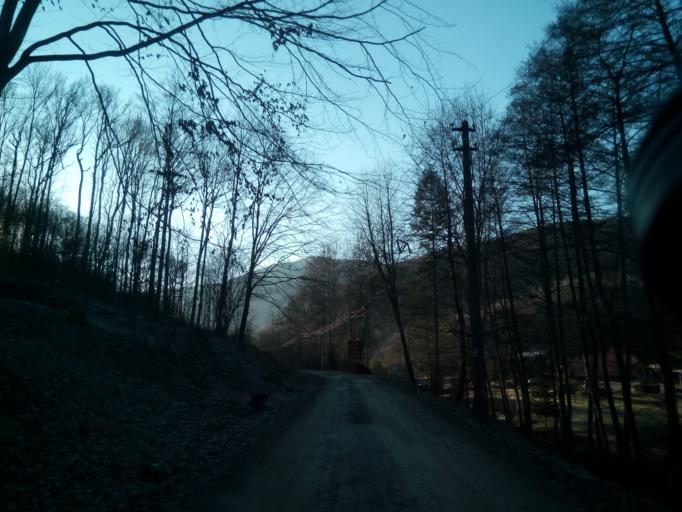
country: SK
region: Kosicky
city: Medzev
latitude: 48.6792
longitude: 20.8834
